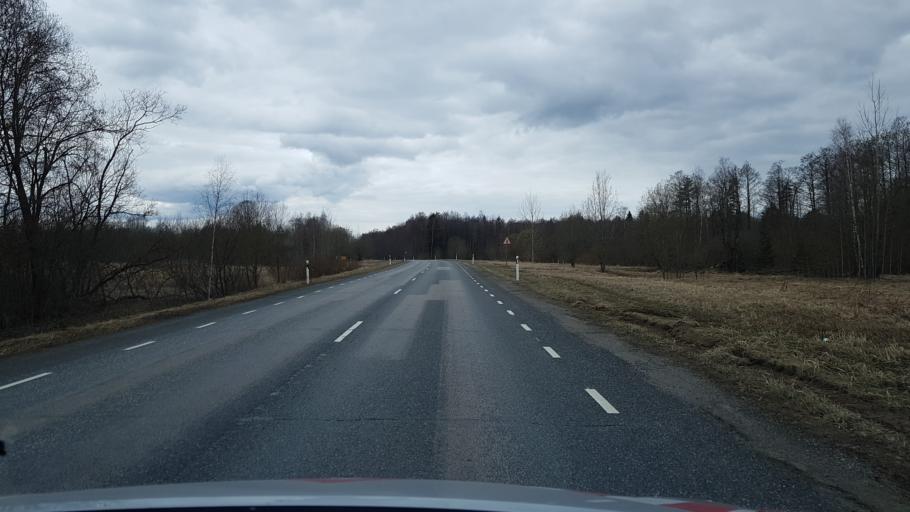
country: EE
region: Ida-Virumaa
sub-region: Narva-Joesuu linn
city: Narva-Joesuu
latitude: 59.3511
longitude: 28.0457
